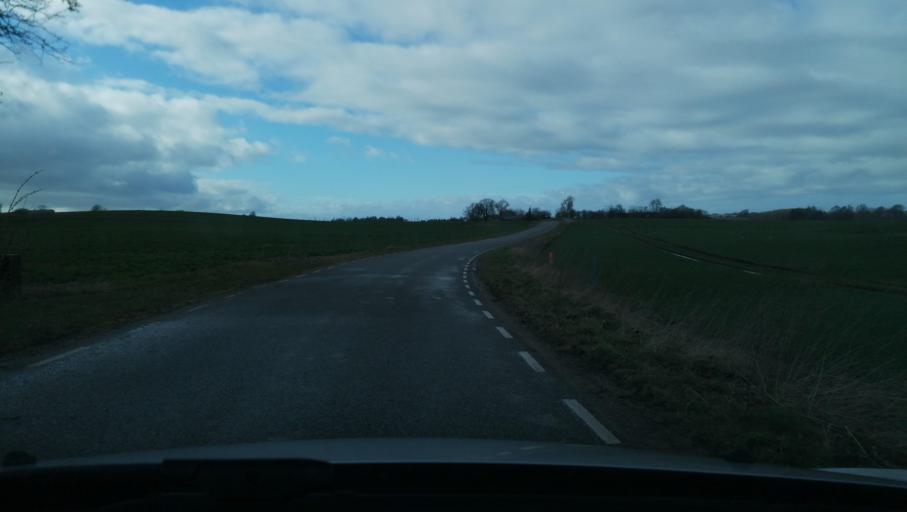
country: DK
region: Zealand
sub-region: Odsherred Kommune
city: Horve
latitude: 55.7464
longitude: 11.3853
